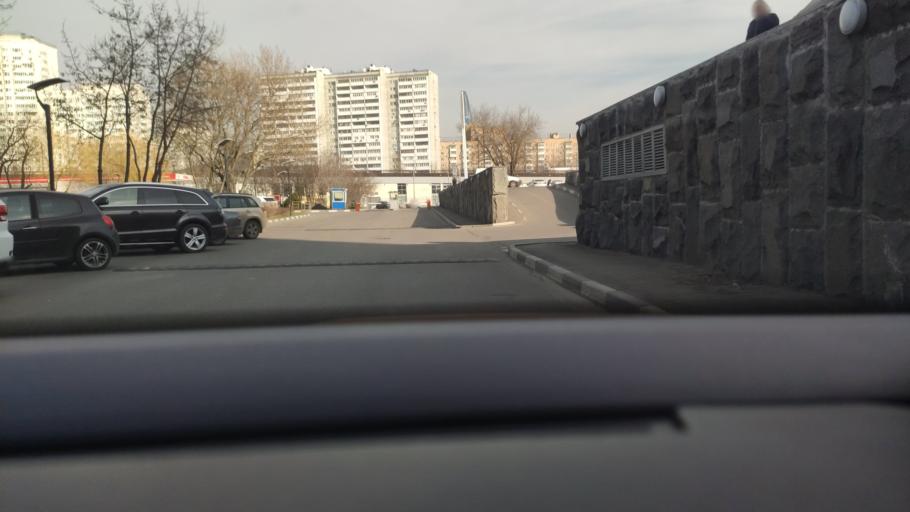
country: RU
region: Moskovskaya
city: Kozhukhovo
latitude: 55.6837
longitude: 37.6617
